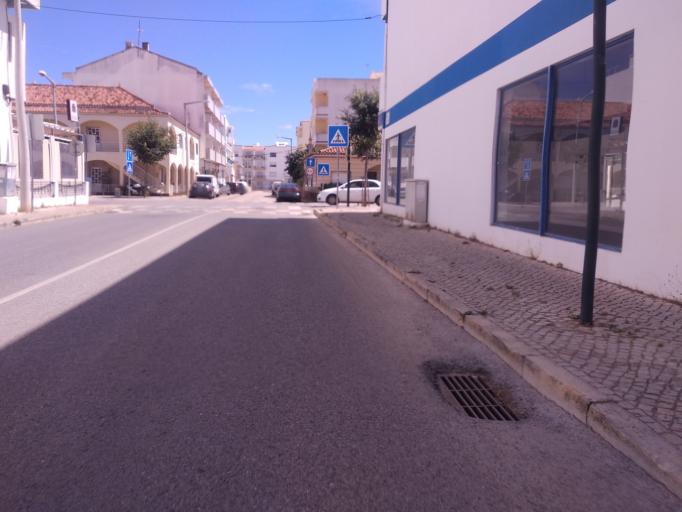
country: PT
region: Faro
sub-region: Sao Bras de Alportel
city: Sao Bras de Alportel
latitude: 37.1530
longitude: -7.8828
